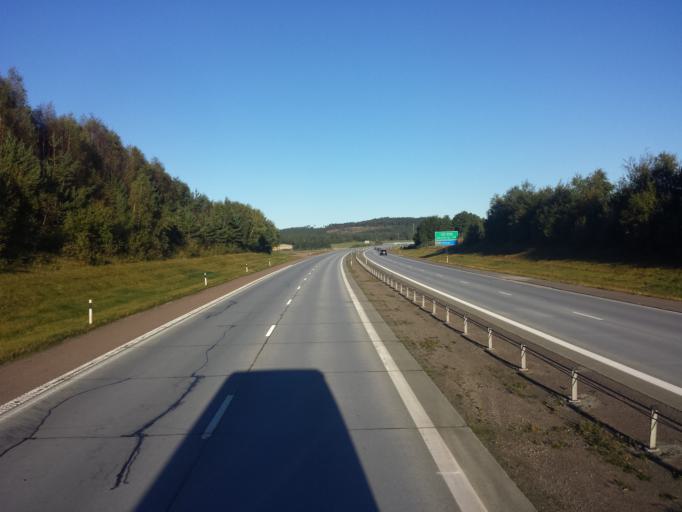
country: SE
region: Halland
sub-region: Halmstads Kommun
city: Getinge
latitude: 56.8079
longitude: 12.7321
